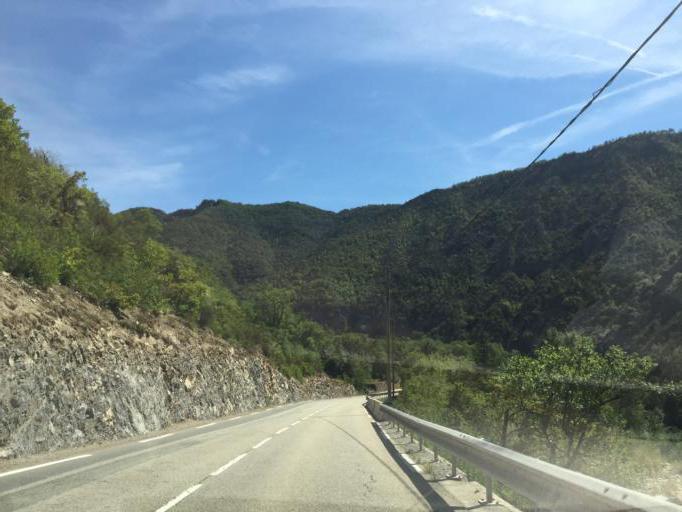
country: FR
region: Provence-Alpes-Cote d'Azur
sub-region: Departement des Alpes-Maritimes
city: Gilette
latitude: 43.9449
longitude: 7.1630
